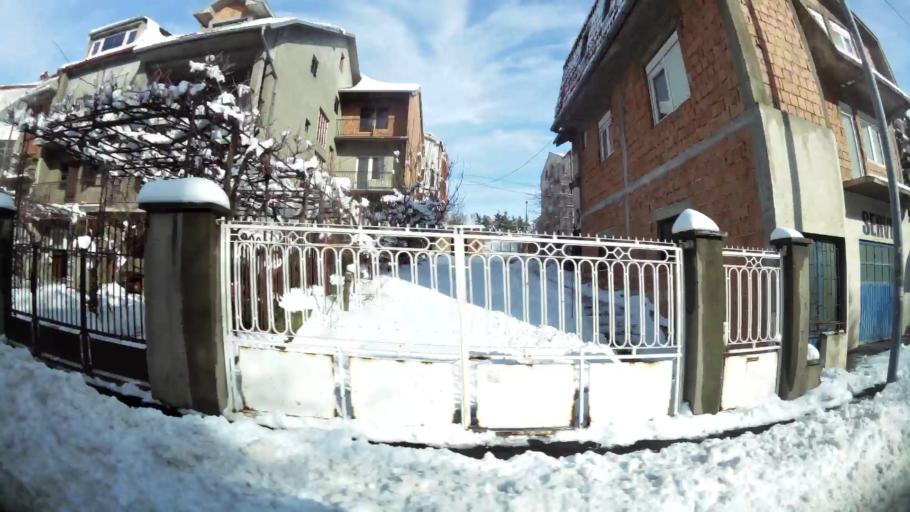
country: RS
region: Central Serbia
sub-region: Belgrade
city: Zvezdara
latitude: 44.7912
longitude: 20.5359
